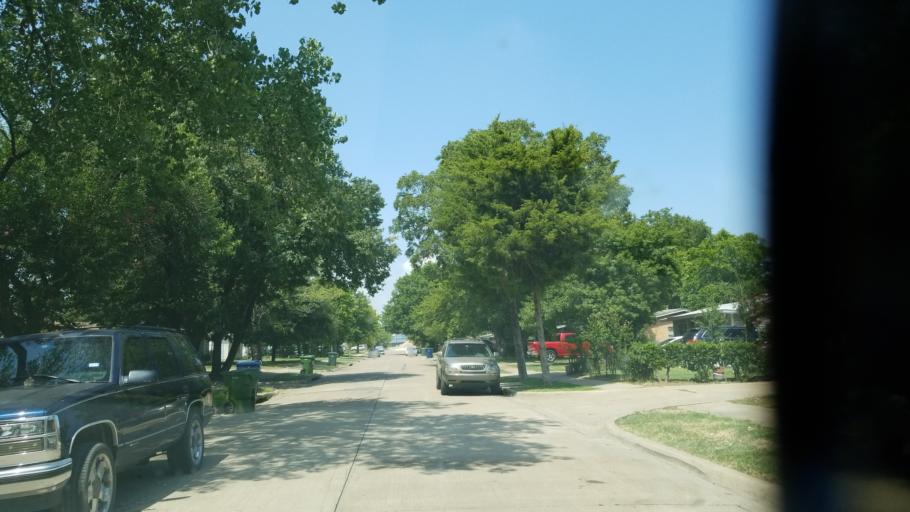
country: US
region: Texas
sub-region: Dallas County
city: Garland
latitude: 32.9191
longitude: -96.6347
